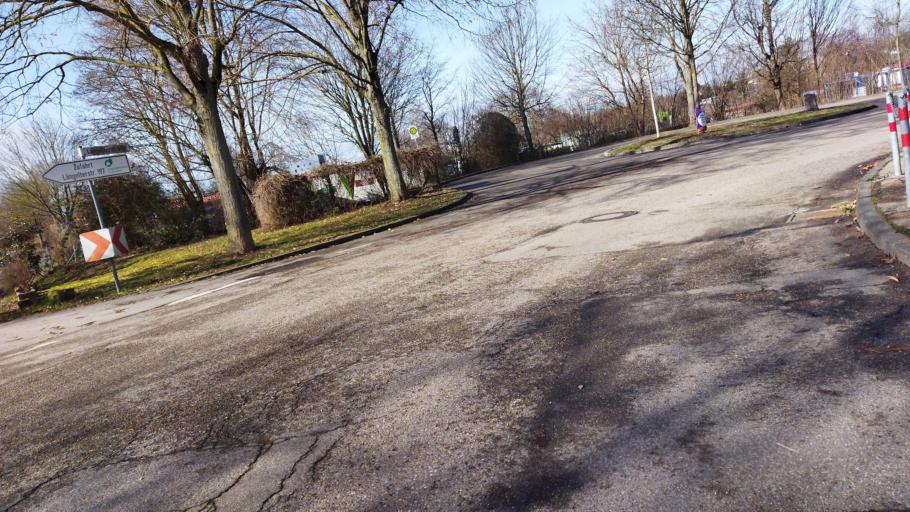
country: DE
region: Baden-Wuerttemberg
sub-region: Regierungsbezirk Stuttgart
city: Heilbronn
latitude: 49.1373
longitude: 9.1710
